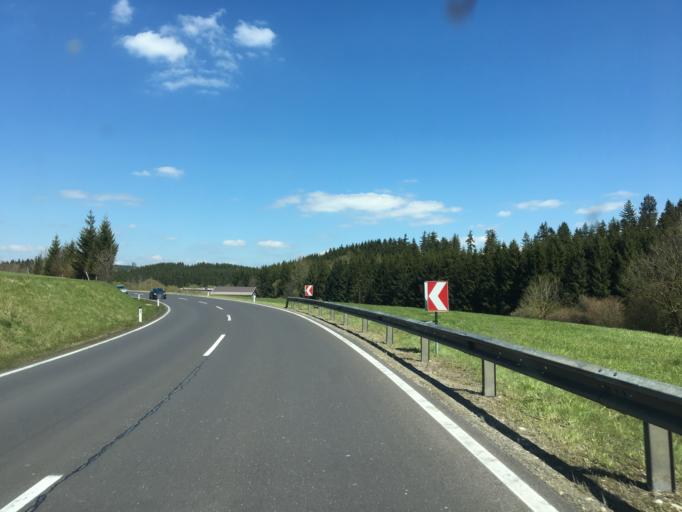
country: AT
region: Upper Austria
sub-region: Politischer Bezirk Urfahr-Umgebung
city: Bad Leonfelden
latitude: 48.4948
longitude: 14.3009
